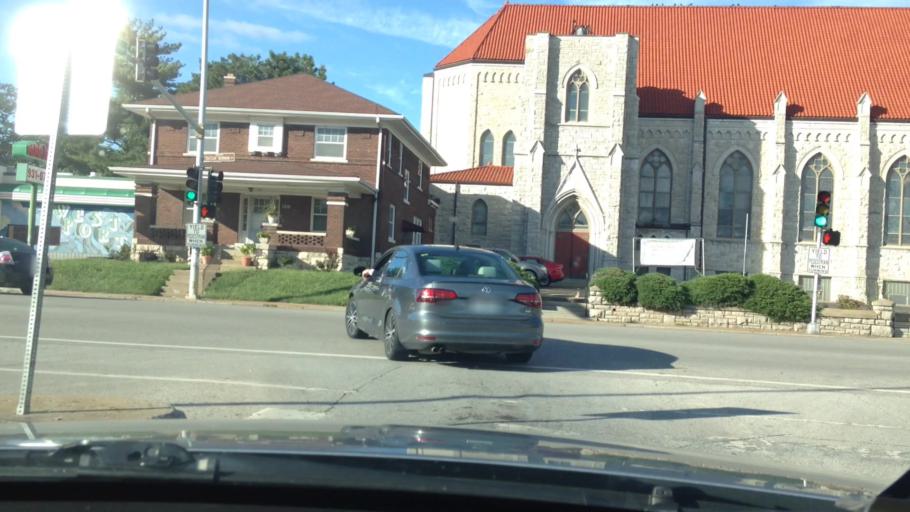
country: US
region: Kansas
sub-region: Johnson County
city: Westwood
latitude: 39.0498
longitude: -94.6026
